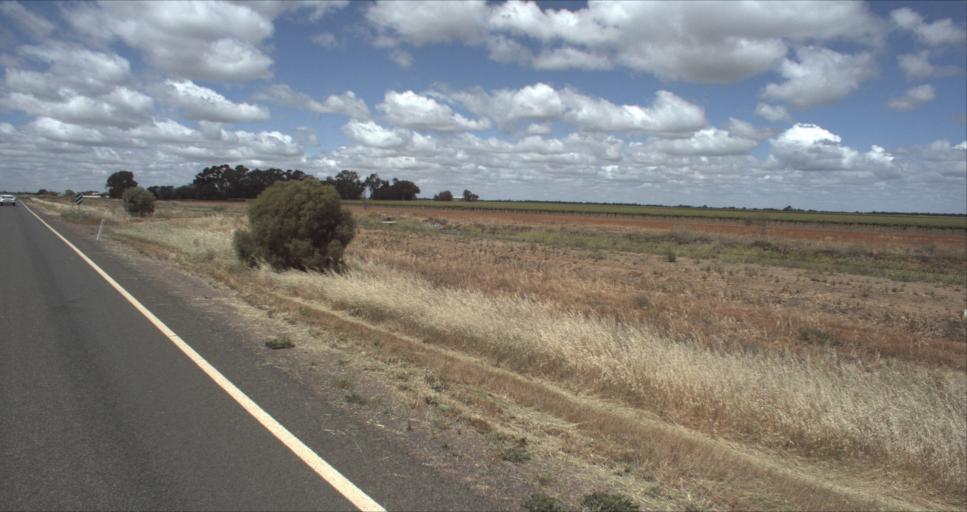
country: AU
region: New South Wales
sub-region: Murrumbidgee Shire
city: Darlington Point
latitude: -34.4808
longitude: 146.1541
